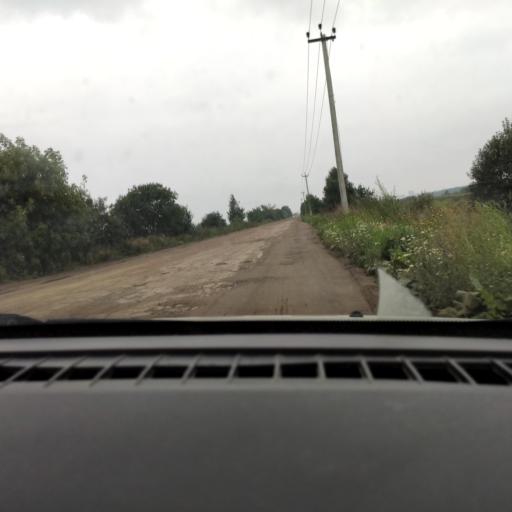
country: RU
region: Perm
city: Kondratovo
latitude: 58.0086
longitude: 56.0481
